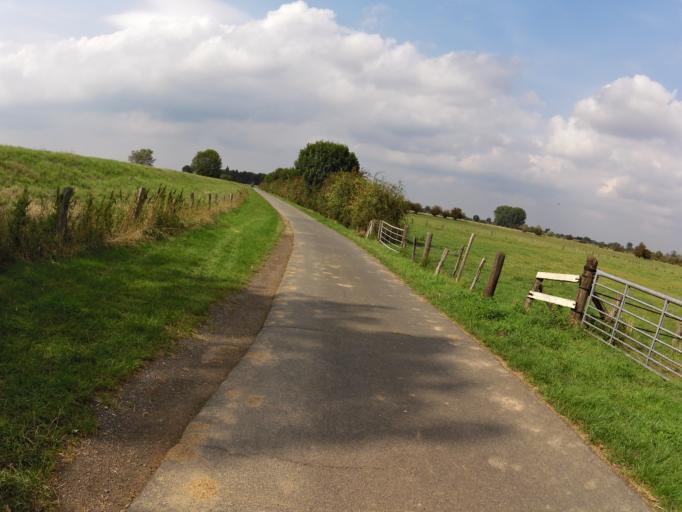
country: DE
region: Lower Saxony
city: Hilgermissen
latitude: 52.8904
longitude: 9.1734
